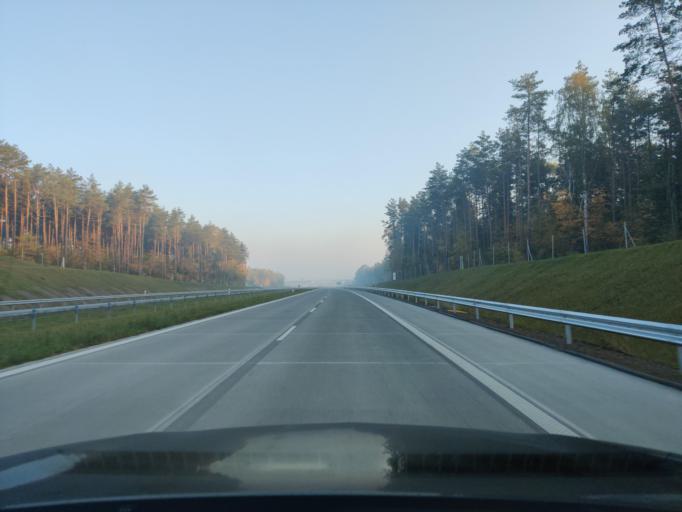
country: PL
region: Masovian Voivodeship
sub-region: Powiat mlawski
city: Mlawa
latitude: 53.1491
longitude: 20.4283
